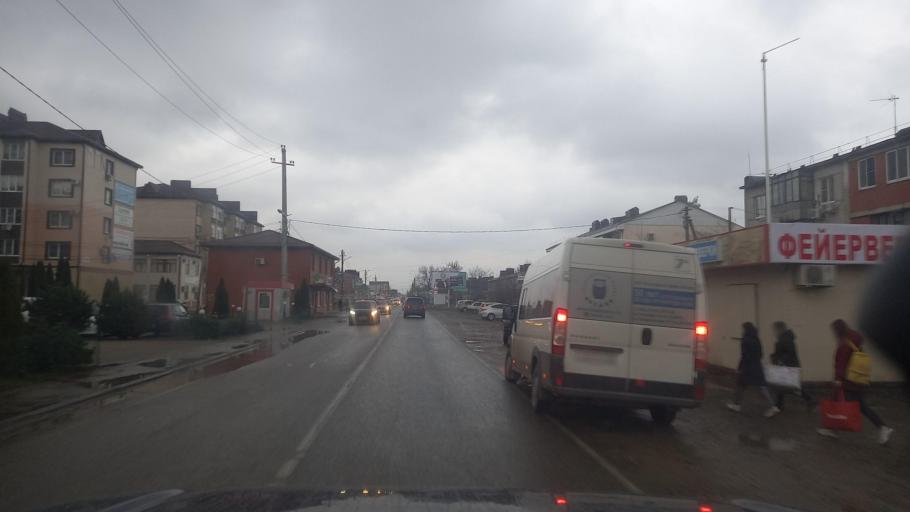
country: RU
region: Adygeya
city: Yablonovskiy
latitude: 44.9915
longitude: 38.9308
